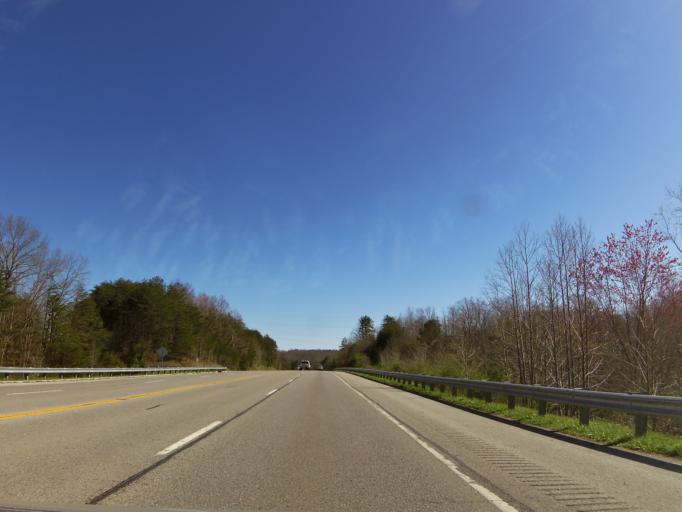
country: US
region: Kentucky
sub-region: McCreary County
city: Stearns
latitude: 36.6898
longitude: -84.4542
